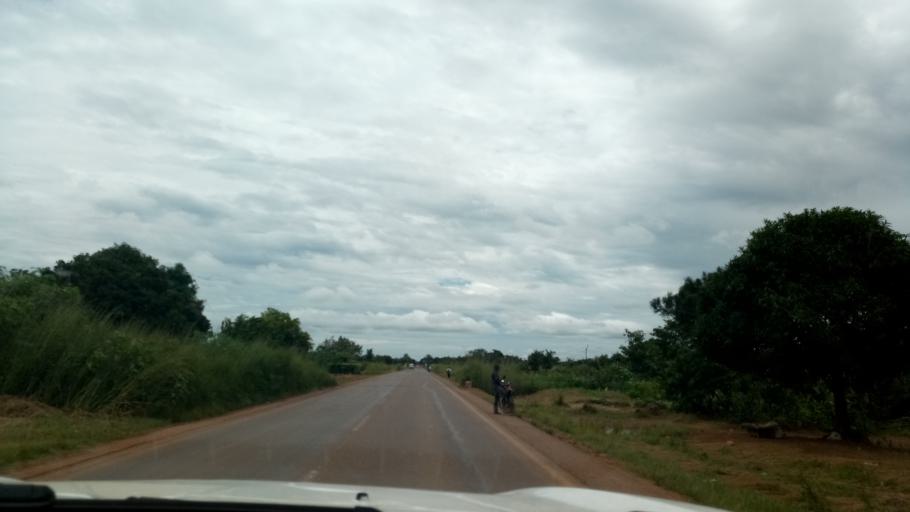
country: CD
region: Katanga
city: Lubumbashi
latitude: -11.5599
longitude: 27.5712
